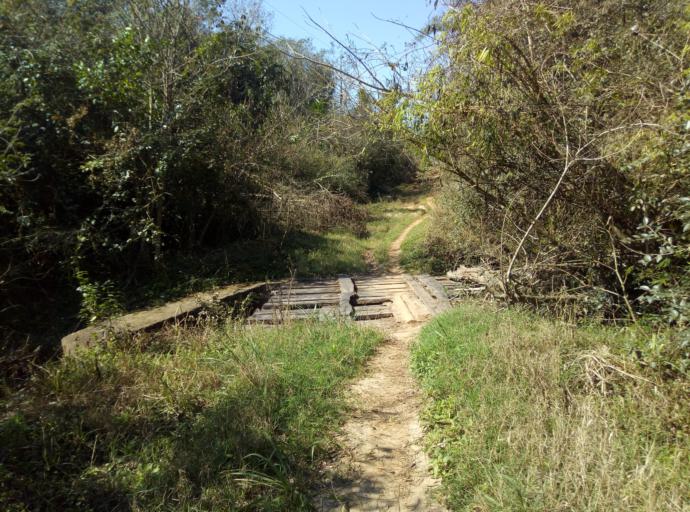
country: PY
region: Caaguazu
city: Doctor Cecilio Baez
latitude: -25.1793
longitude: -56.2223
